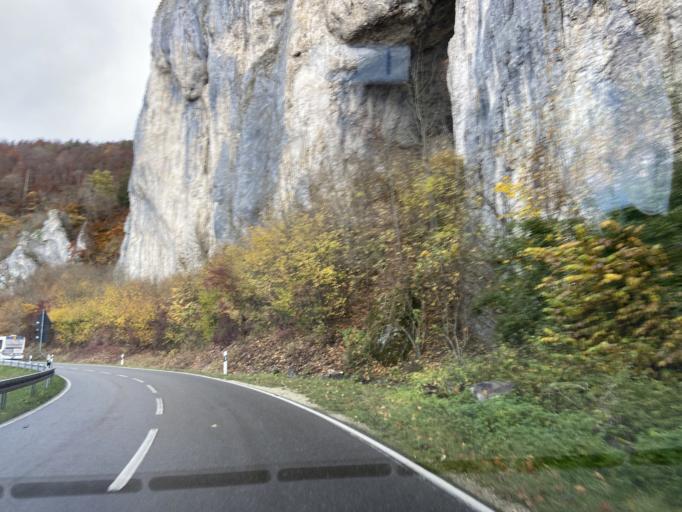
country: DE
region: Baden-Wuerttemberg
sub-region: Tuebingen Region
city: Stetten am Kalten Markt
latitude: 48.0933
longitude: 9.1080
